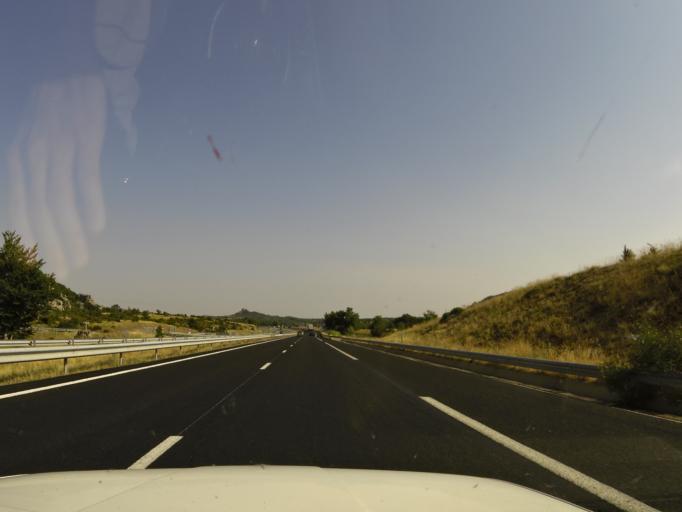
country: FR
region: Midi-Pyrenees
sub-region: Departement de l'Aveyron
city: La Cavalerie
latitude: 43.8964
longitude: 3.2809
